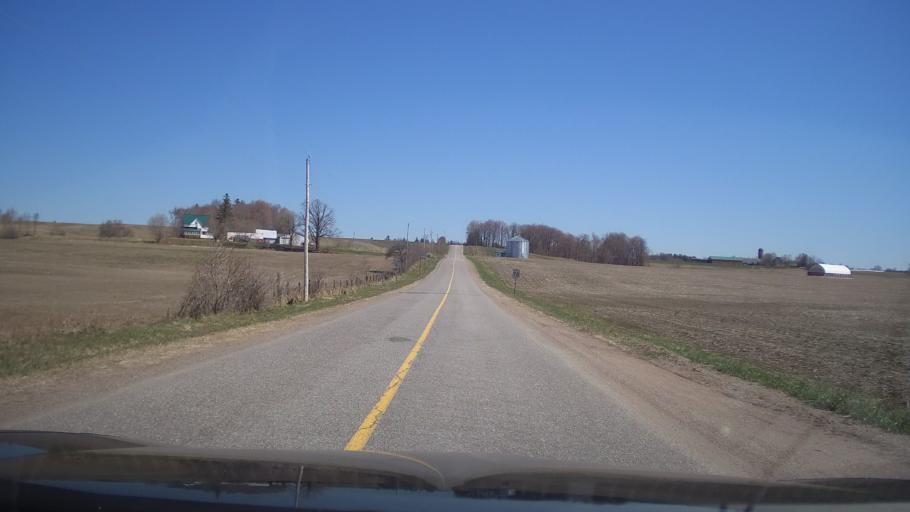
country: CA
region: Ontario
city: Arnprior
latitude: 45.5311
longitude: -76.3955
